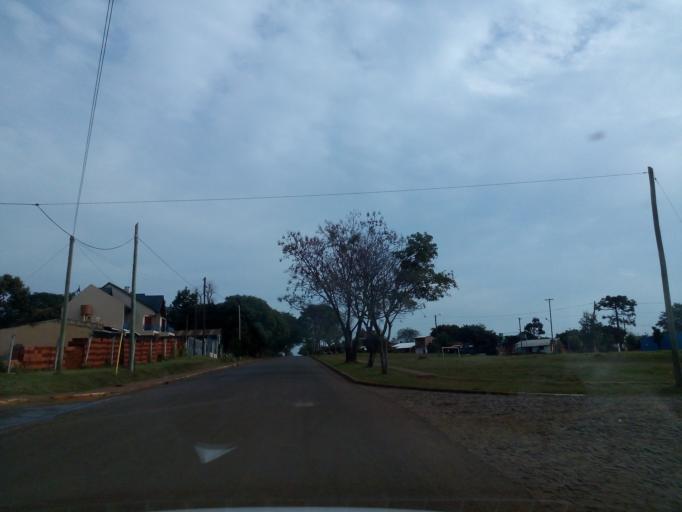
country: AR
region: Misiones
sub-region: Departamento de Capital
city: Posadas
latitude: -27.4239
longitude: -55.8832
